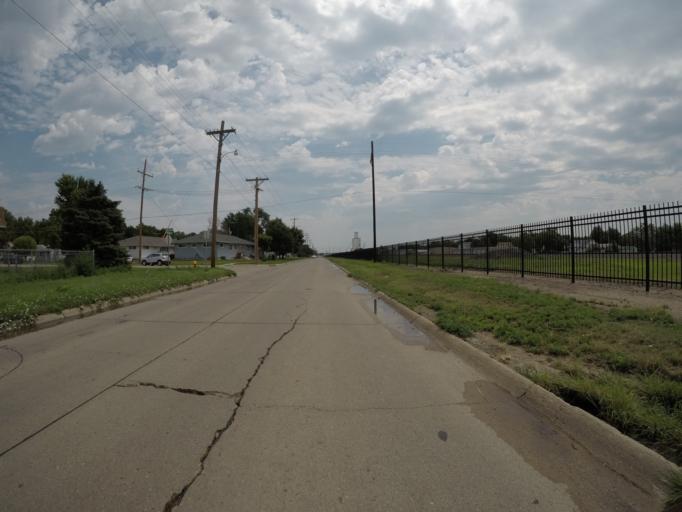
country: US
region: Nebraska
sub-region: Buffalo County
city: Kearney
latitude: 40.6942
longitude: -99.0945
